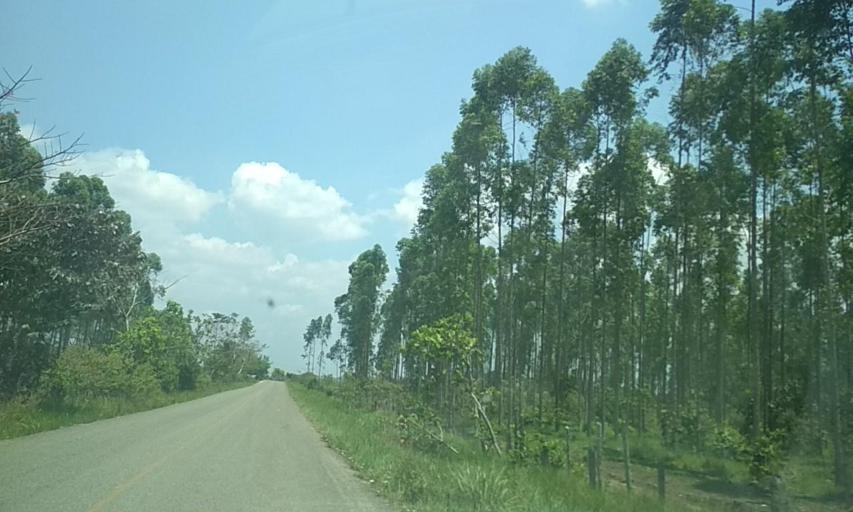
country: MX
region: Tabasco
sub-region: Huimanguillo
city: Francisco Rueda
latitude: 17.8323
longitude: -93.8750
